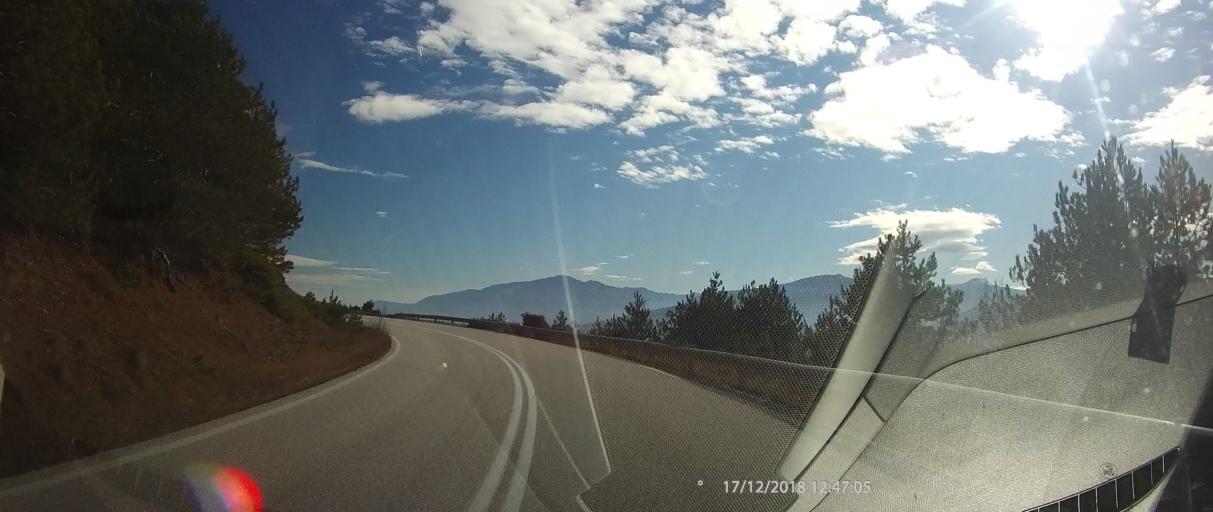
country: GR
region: Thessaly
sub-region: Trikala
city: Kastraki
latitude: 39.7862
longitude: 21.4235
